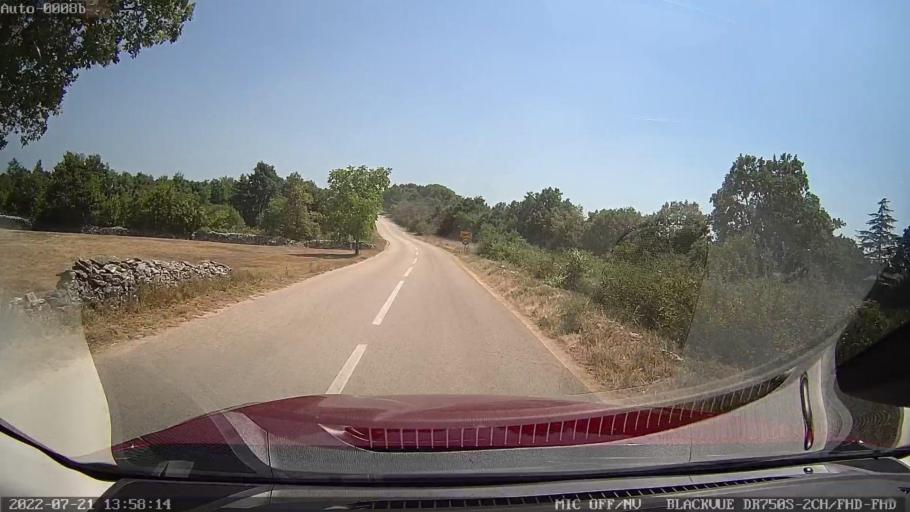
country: HR
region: Istarska
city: Vodnjan
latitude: 45.1111
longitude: 13.8530
